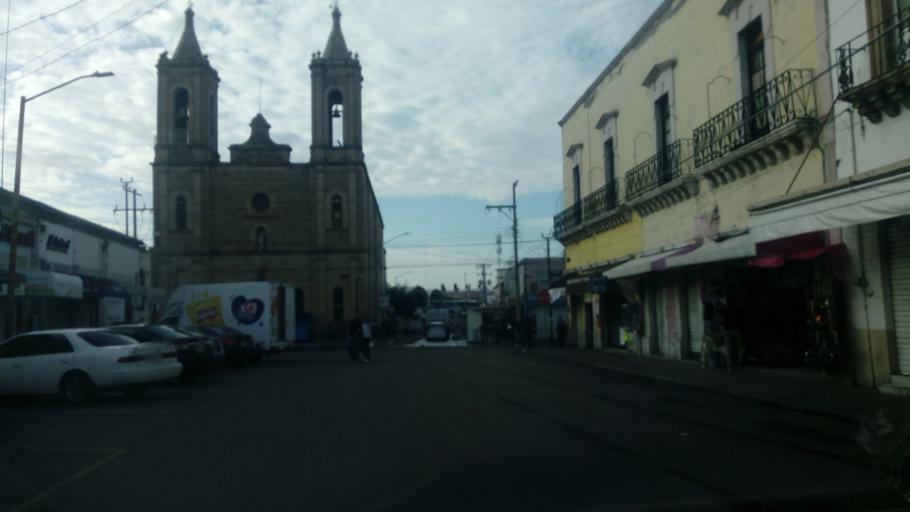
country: MX
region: Durango
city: Victoria de Durango
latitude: 24.0230
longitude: -104.6672
